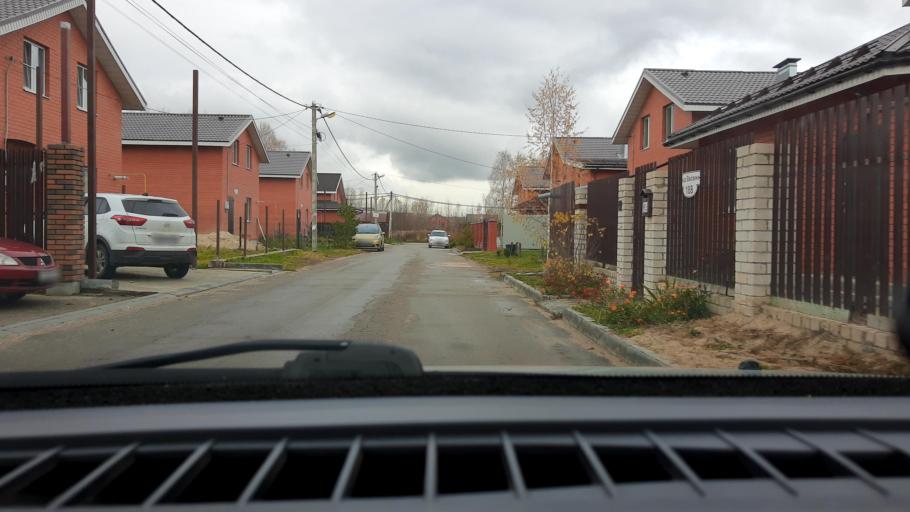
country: RU
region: Nizjnij Novgorod
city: Afonino
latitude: 56.2038
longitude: 44.1250
